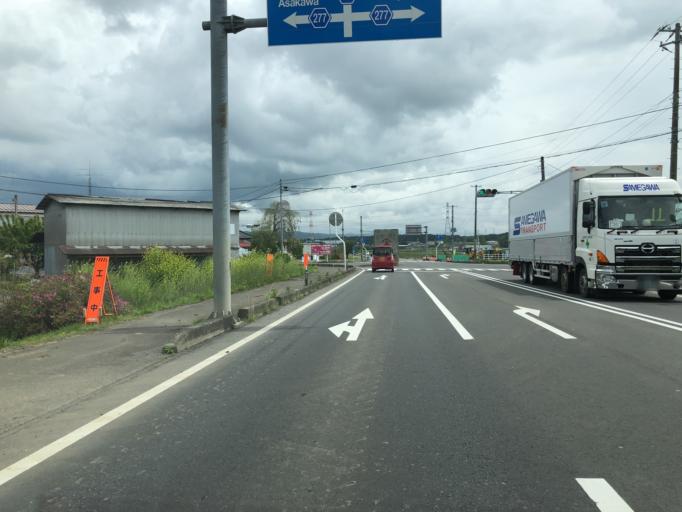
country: JP
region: Fukushima
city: Ishikawa
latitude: 37.0681
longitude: 140.3695
